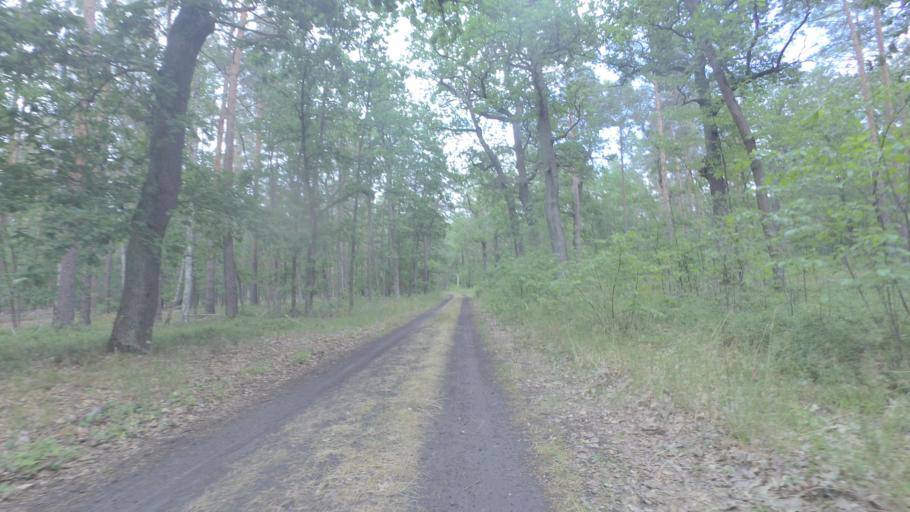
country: DE
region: Brandenburg
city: Am Mellensee
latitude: 52.1304
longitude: 13.4440
